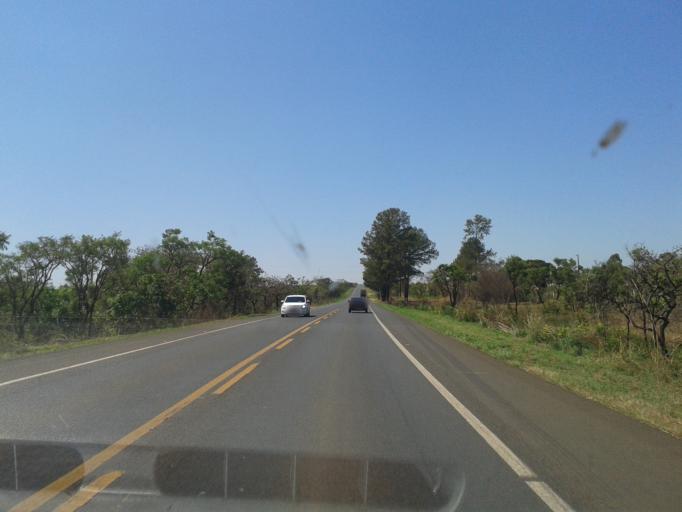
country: BR
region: Minas Gerais
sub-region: Uberaba
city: Uberaba
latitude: -19.2918
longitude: -47.6019
